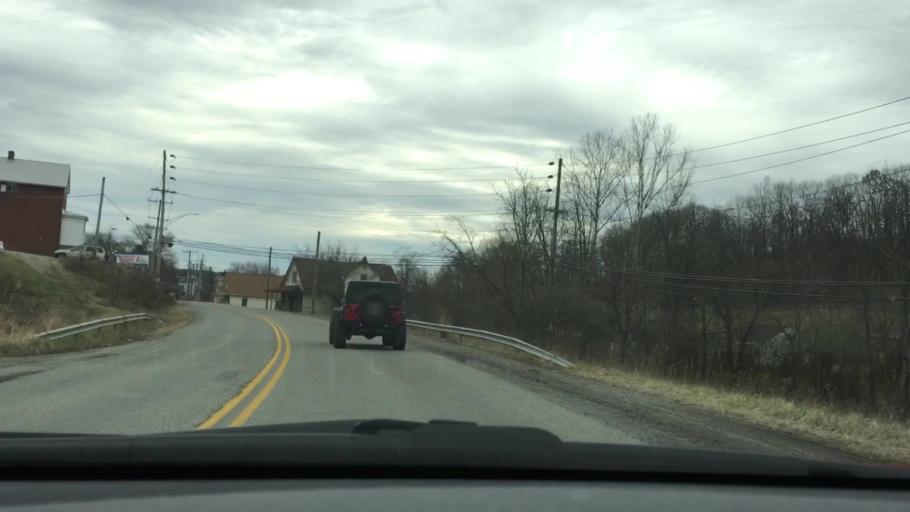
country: US
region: Pennsylvania
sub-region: Washington County
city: Midland
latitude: 40.2579
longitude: -80.2175
